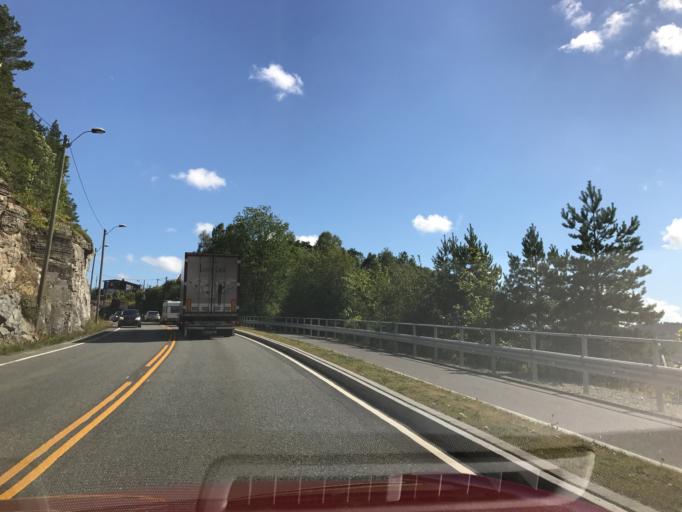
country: NO
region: Telemark
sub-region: Bamble
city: Langesund
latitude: 59.0576
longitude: 9.6893
